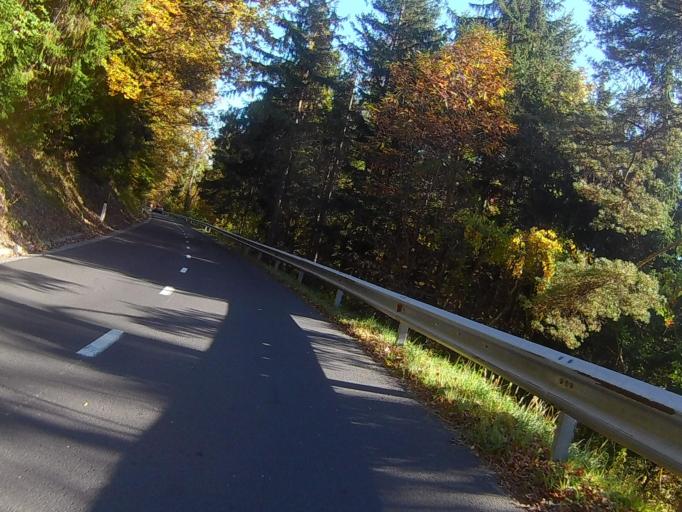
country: SI
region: Race-Fram
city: Morje
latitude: 46.4858
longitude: 15.5724
